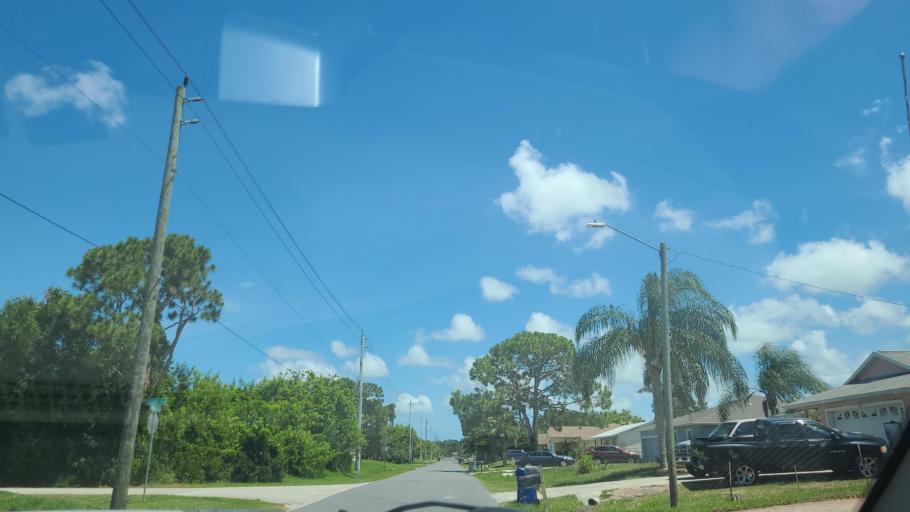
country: US
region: Florida
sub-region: Indian River County
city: Sebastian
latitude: 27.7842
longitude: -80.4842
